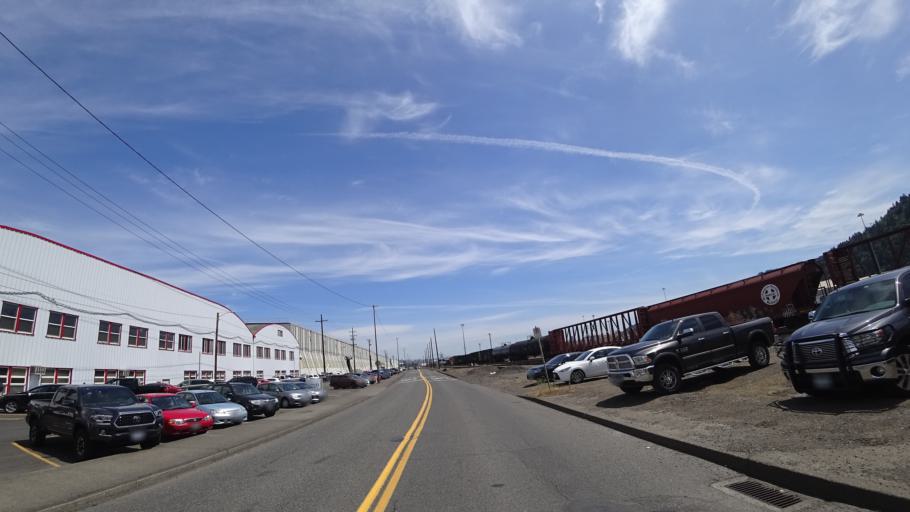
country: US
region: Oregon
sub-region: Washington County
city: West Haven-Sylvan
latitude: 45.5562
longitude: -122.7268
